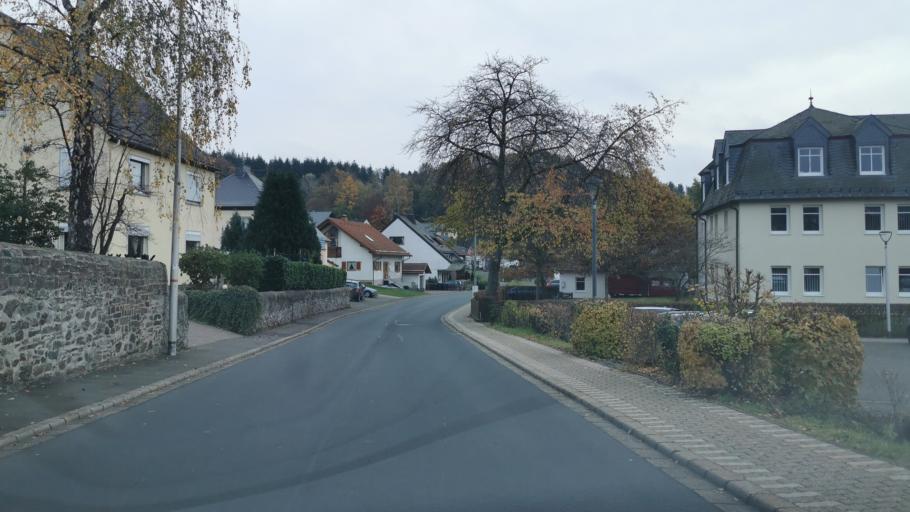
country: DE
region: Rheinland-Pfalz
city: Ulmen
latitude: 50.2074
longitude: 6.9810
